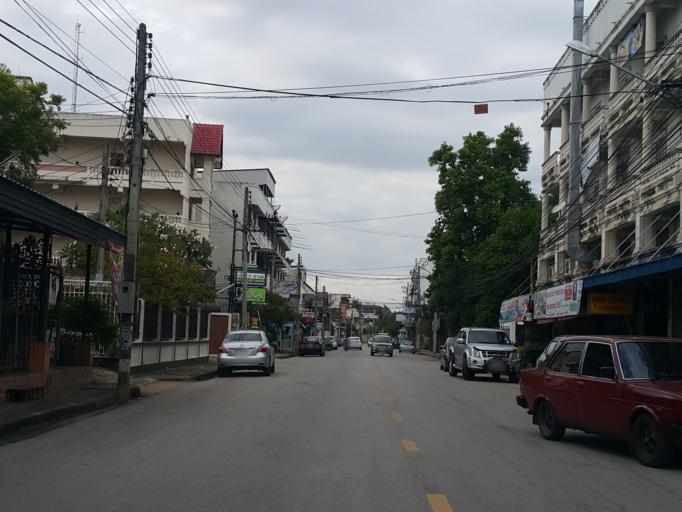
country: TH
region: Lampang
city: Lampang
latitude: 18.2812
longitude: 99.4781
